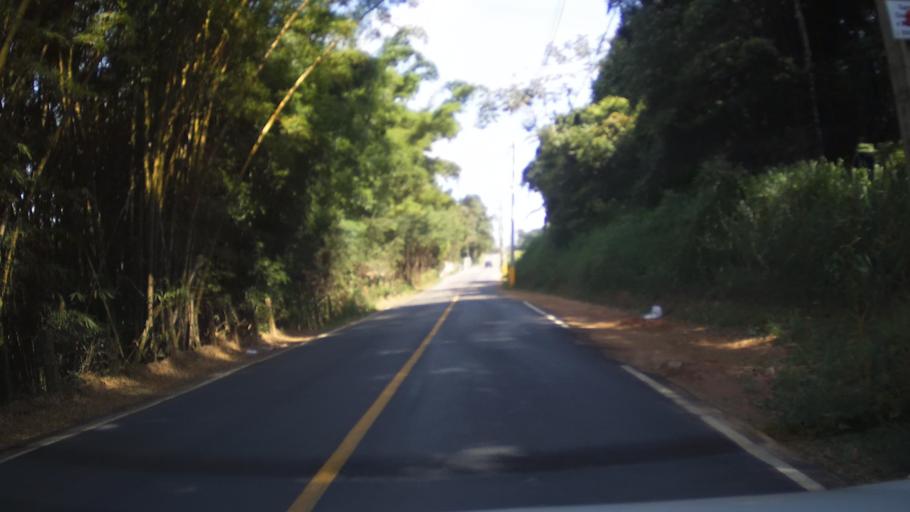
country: BR
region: Sao Paulo
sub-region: Itupeva
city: Itupeva
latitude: -23.1994
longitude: -47.0688
